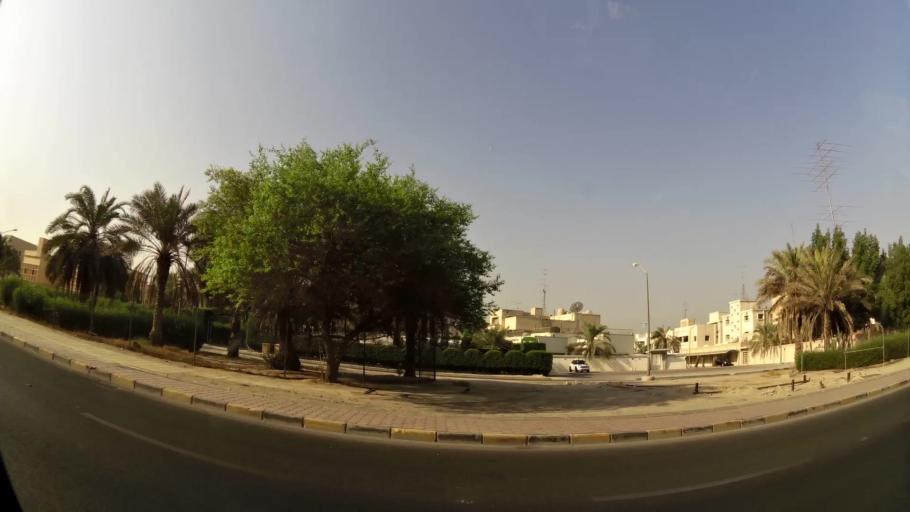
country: KW
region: Muhafazat Hawalli
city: Hawalli
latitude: 29.3525
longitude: 48.0259
